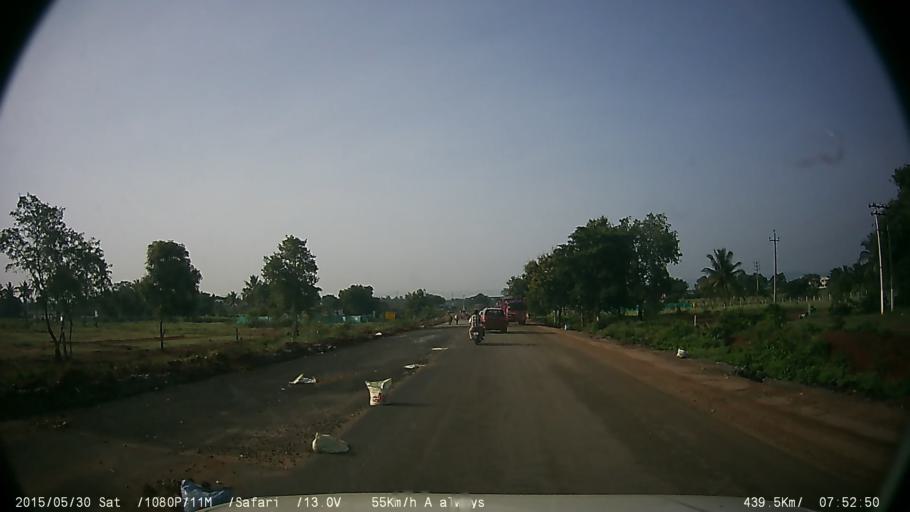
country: IN
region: Karnataka
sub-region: Chamrajnagar
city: Gundlupet
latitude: 11.8270
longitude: 76.6798
